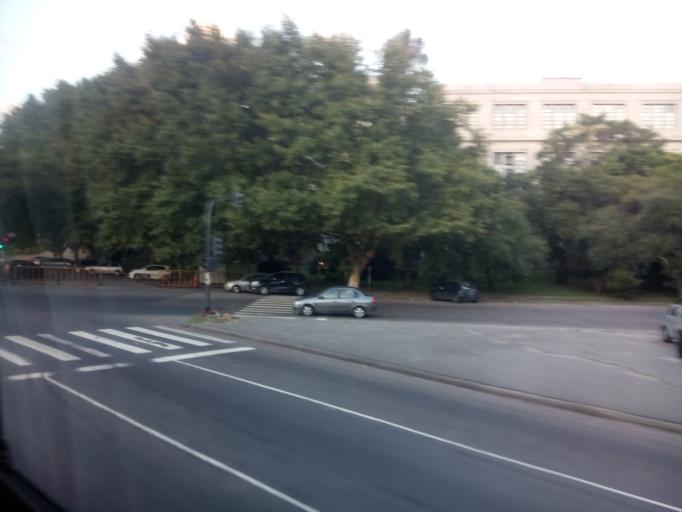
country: AR
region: Buenos Aires F.D.
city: Retiro
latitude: -34.5848
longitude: -58.3727
